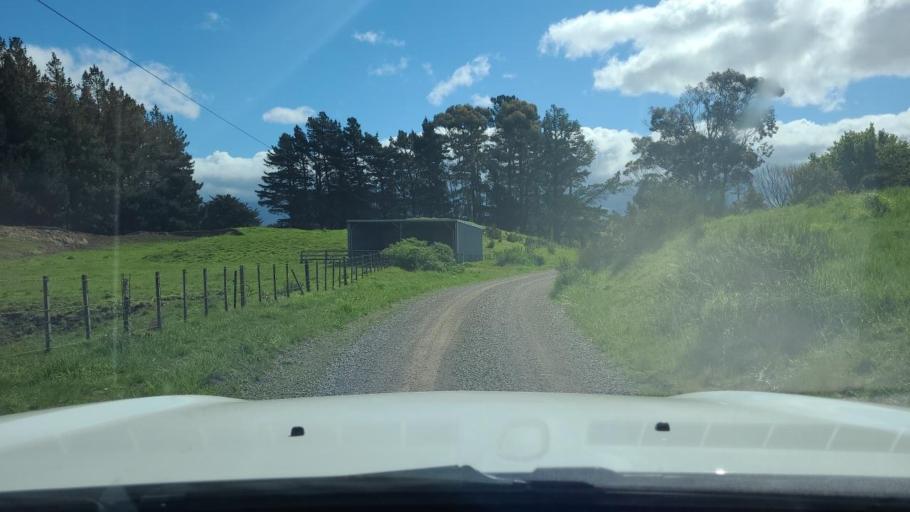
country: NZ
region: Wellington
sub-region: Upper Hutt City
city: Upper Hutt
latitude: -41.2352
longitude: 175.2927
